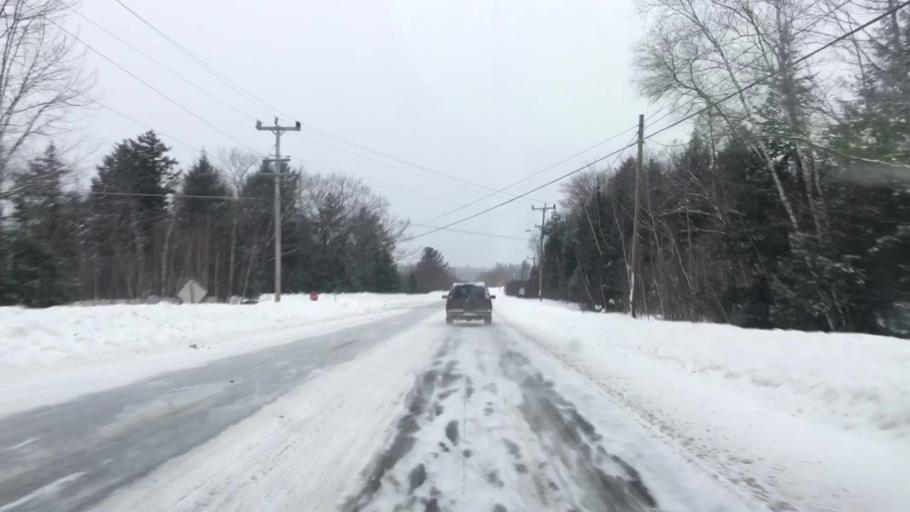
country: US
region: Maine
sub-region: Penobscot County
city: Medway
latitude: 45.5952
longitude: -68.4850
